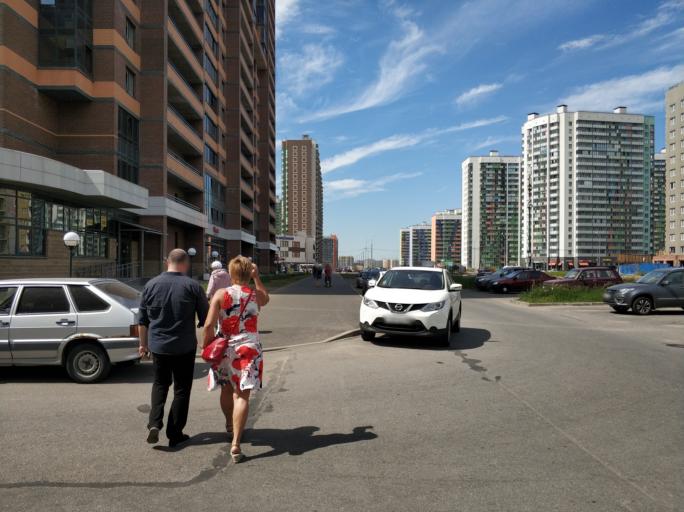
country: RU
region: Leningrad
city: Murino
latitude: 60.0570
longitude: 30.4320
